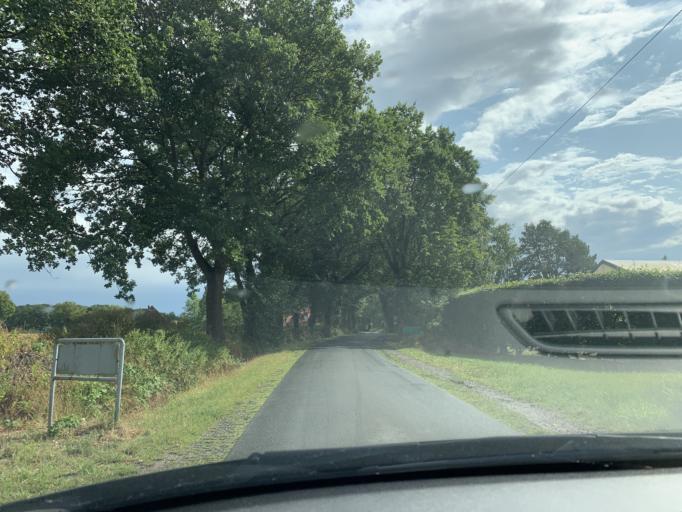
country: DE
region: Lower Saxony
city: Westerstede
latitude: 53.2610
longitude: 7.9008
